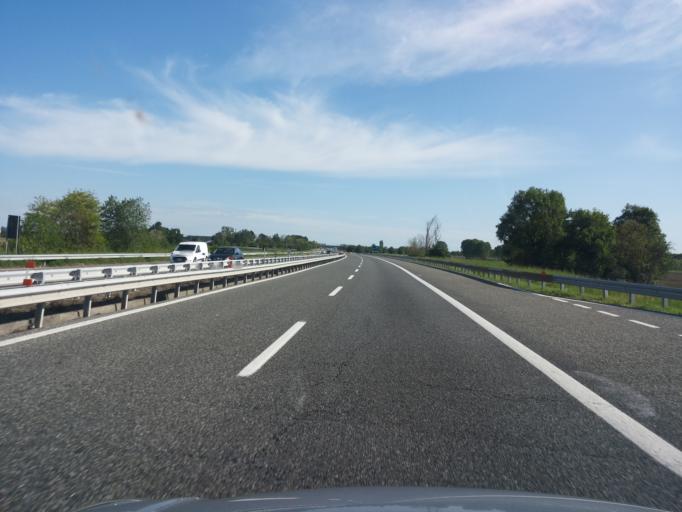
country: IT
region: Piedmont
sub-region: Provincia di Novara
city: Sillavengo
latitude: 45.5092
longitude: 8.4333
